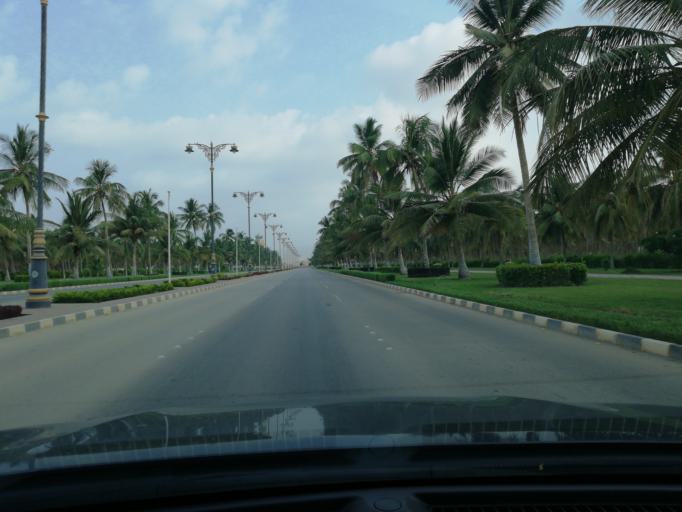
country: OM
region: Zufar
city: Salalah
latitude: 17.0330
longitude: 54.1088
